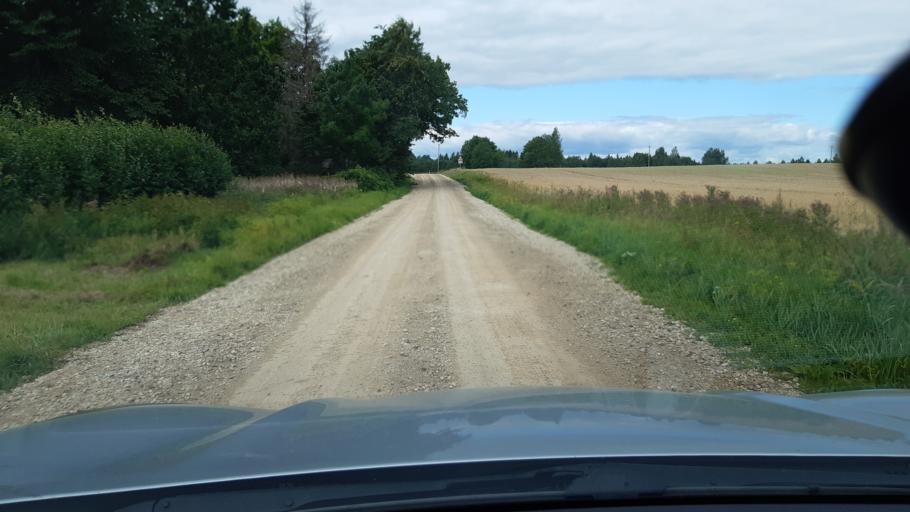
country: EE
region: Raplamaa
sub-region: Jaervakandi vald
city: Jarvakandi
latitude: 58.8047
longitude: 24.8487
